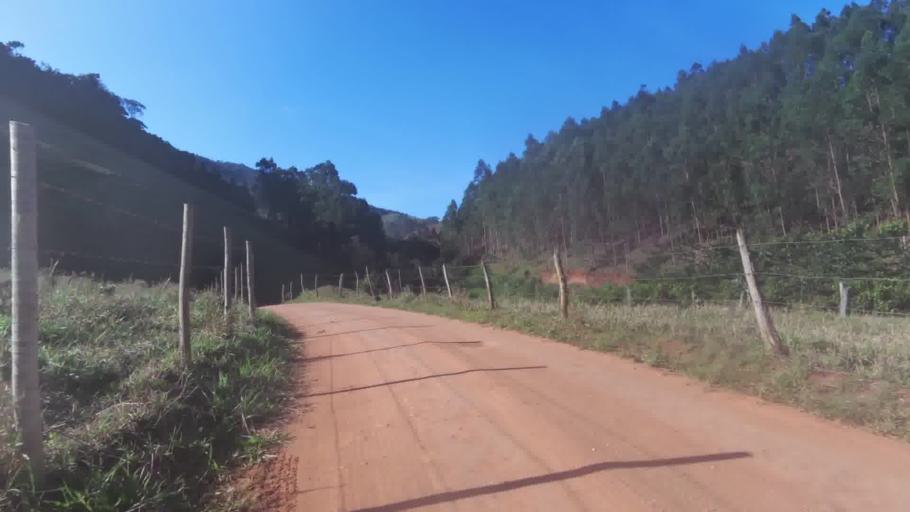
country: BR
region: Espirito Santo
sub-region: Iconha
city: Iconha
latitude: -20.7445
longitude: -40.7967
